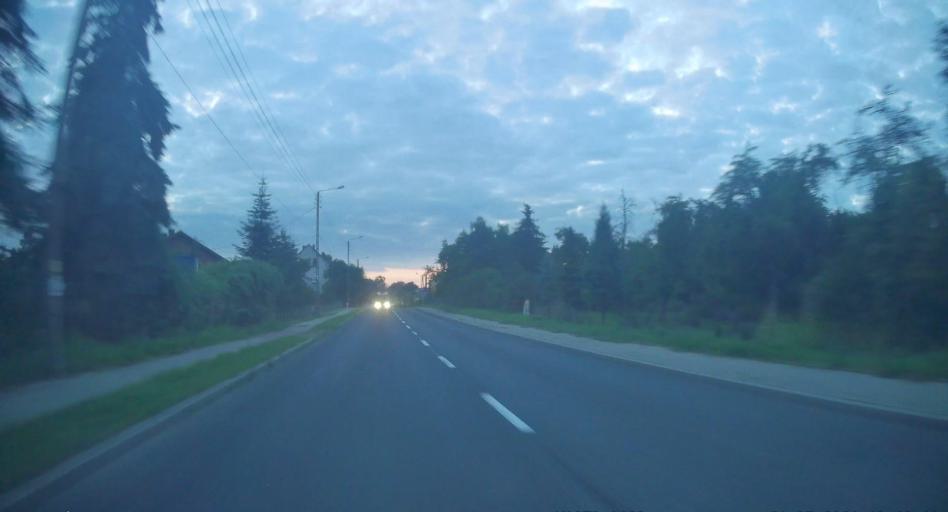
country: PL
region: Opole Voivodeship
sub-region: Powiat oleski
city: Dalachow
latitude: 51.0363
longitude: 18.6072
